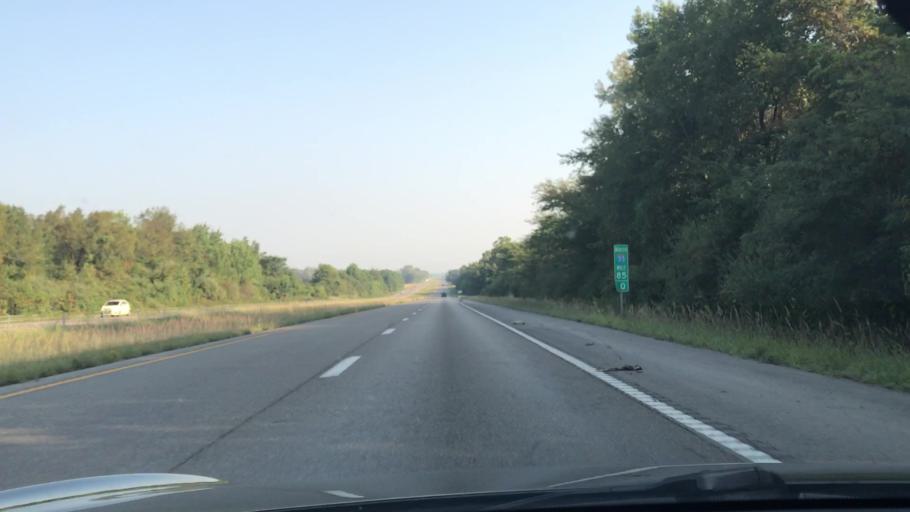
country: US
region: Missouri
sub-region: Scott County
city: Benton
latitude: 37.1469
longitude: -89.5369
